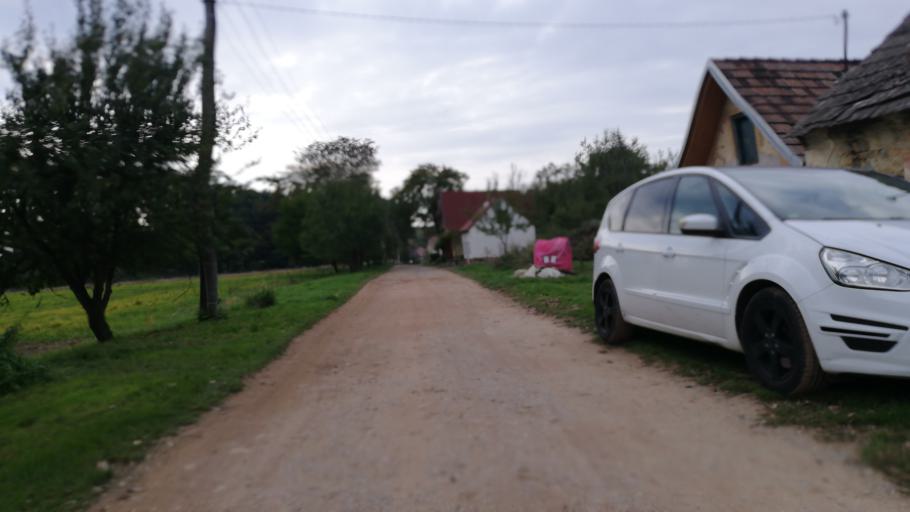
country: SK
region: Trnavsky
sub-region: Okres Skalica
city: Skalica
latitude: 48.8168
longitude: 17.2494
